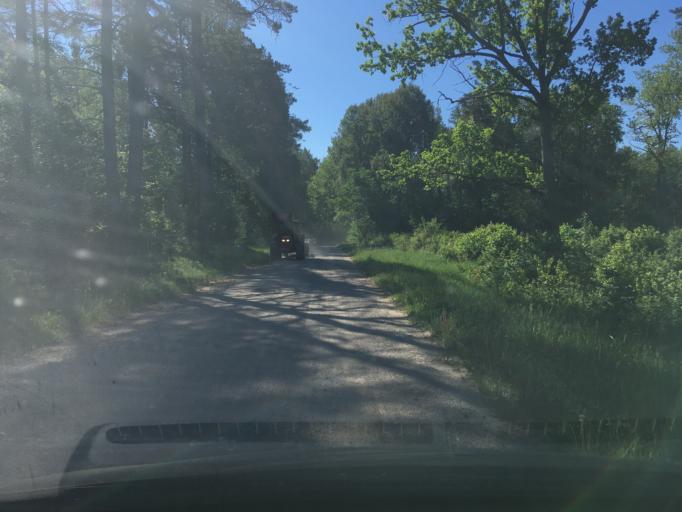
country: EE
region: Laeaene
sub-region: Lihula vald
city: Lihula
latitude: 58.6441
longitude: 23.7862
